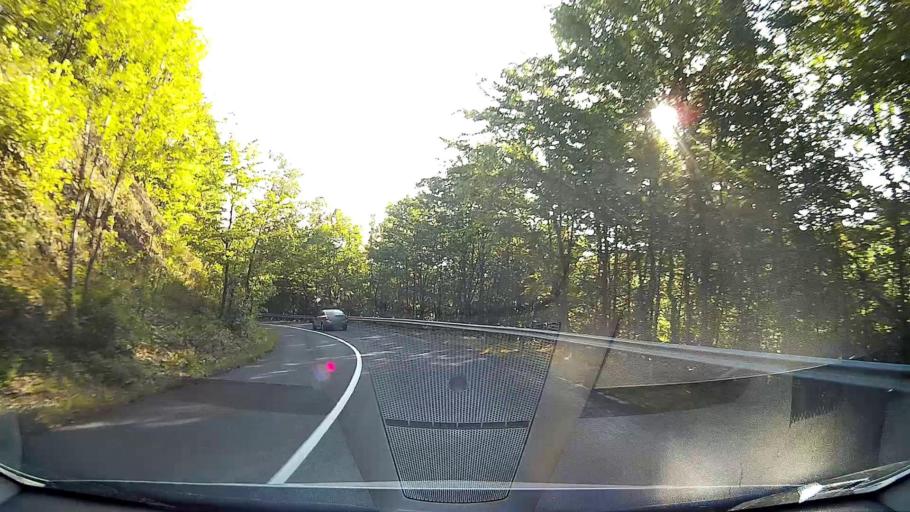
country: HU
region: Pest
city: Visegrad
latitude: 47.7297
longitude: 18.9544
